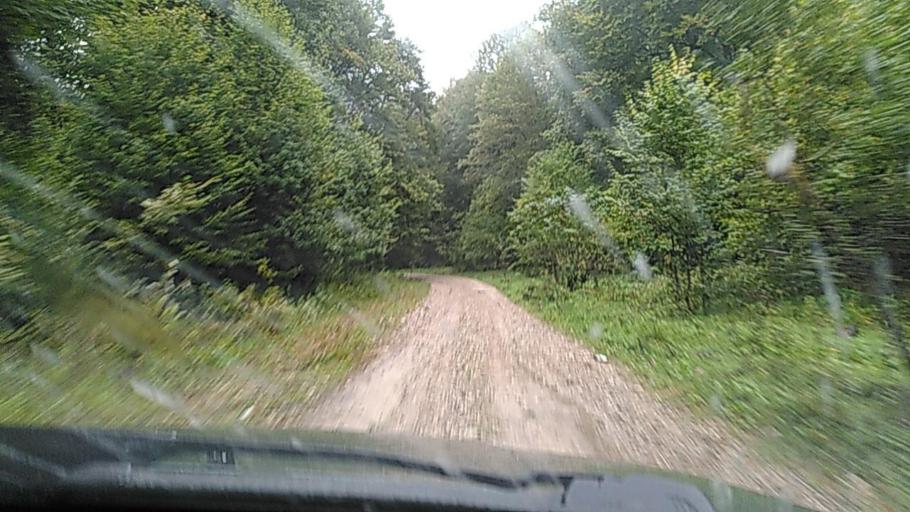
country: RU
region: Kabardino-Balkariya
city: Belaya Rechka
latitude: 43.3928
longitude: 43.4427
